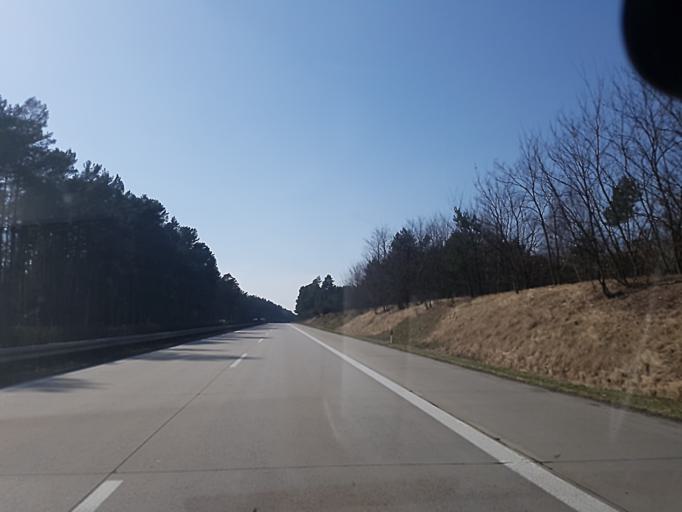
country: DE
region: Brandenburg
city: Heinersbruck
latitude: 51.7097
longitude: 14.5240
